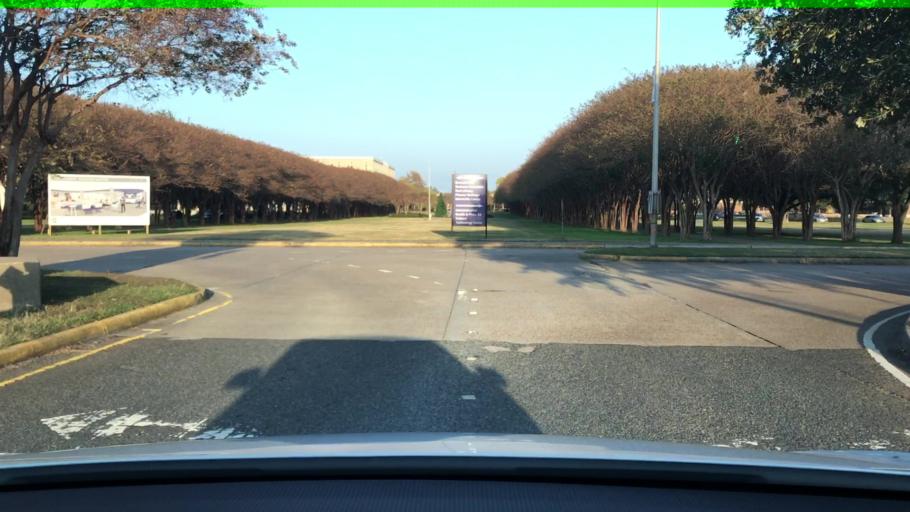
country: US
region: Louisiana
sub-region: Bossier Parish
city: Bossier City
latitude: 32.4267
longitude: -93.7085
